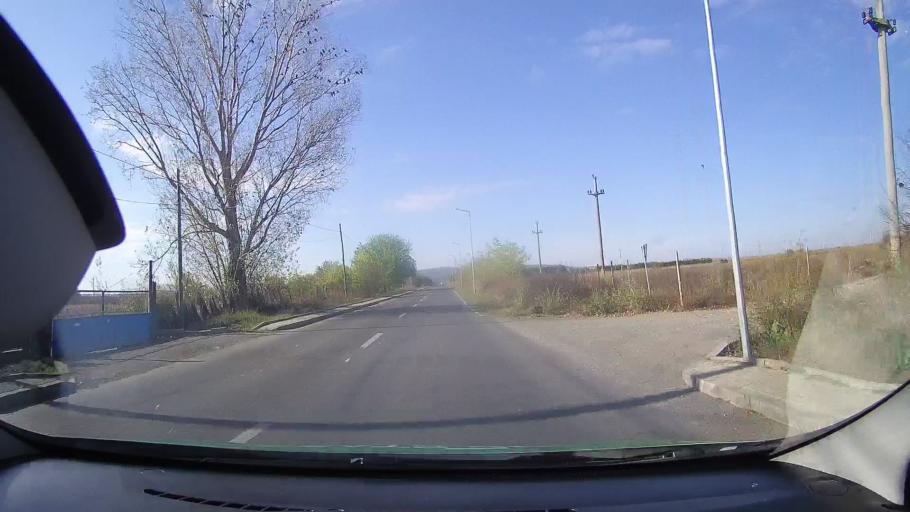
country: RO
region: Tulcea
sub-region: Comuna Valea Nucarilor
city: Valea Nucarilor
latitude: 45.0408
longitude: 28.9261
